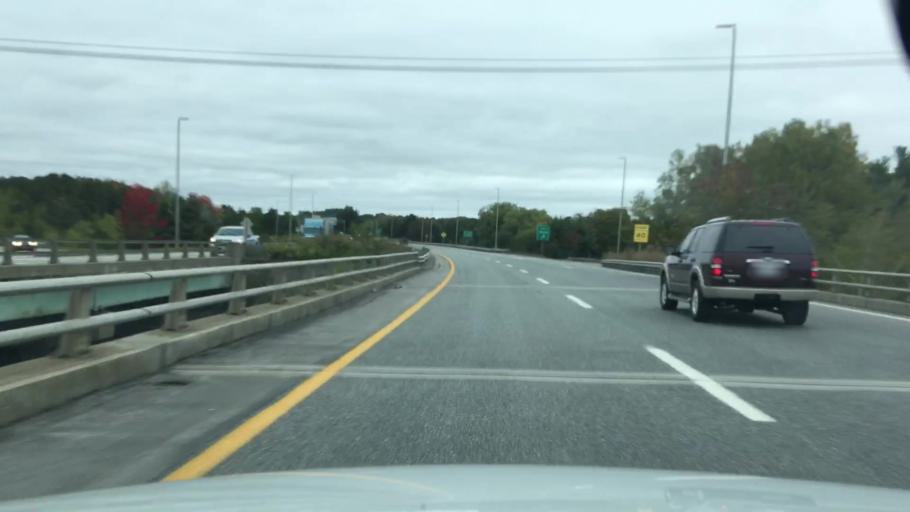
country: US
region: Maine
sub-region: Penobscot County
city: Bangor
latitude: 44.7838
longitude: -68.8109
